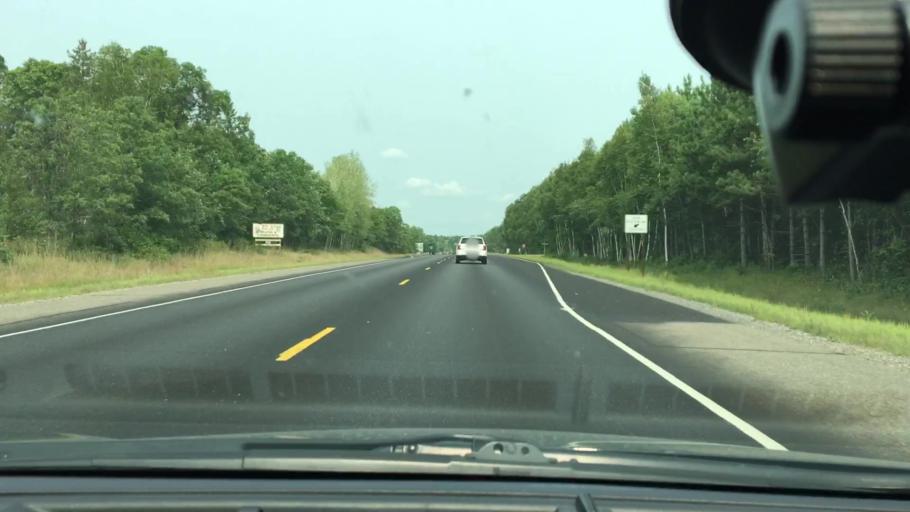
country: US
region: Minnesota
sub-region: Crow Wing County
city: Cross Lake
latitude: 46.6331
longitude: -94.1233
